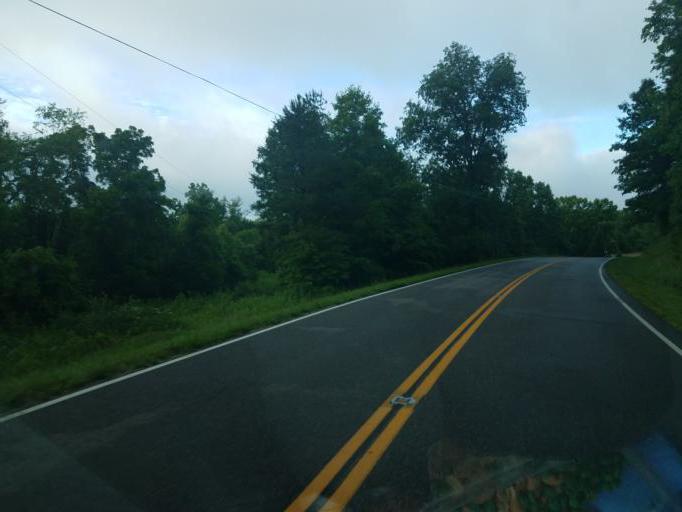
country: US
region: Ohio
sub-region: Gallia County
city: Gallipolis
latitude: 38.8693
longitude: -82.3799
